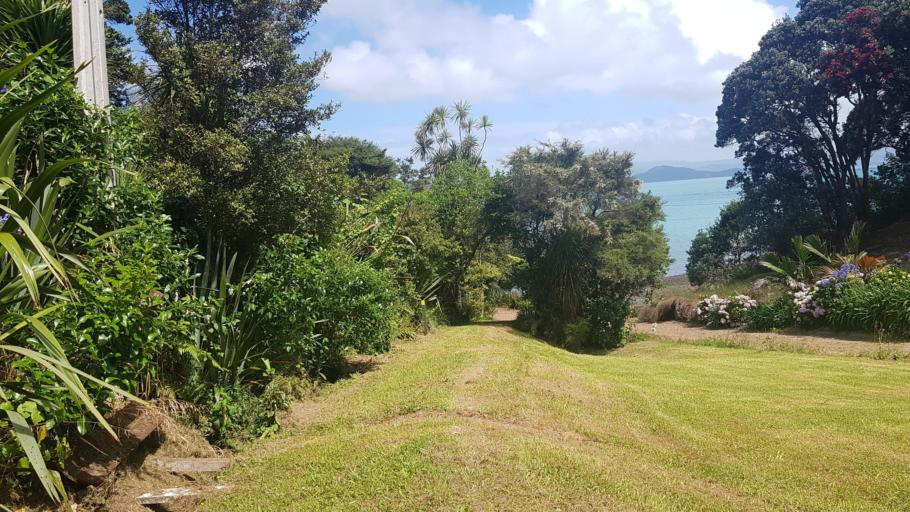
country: NZ
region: Auckland
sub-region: Auckland
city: Pakuranga
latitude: -36.8442
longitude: 175.1467
